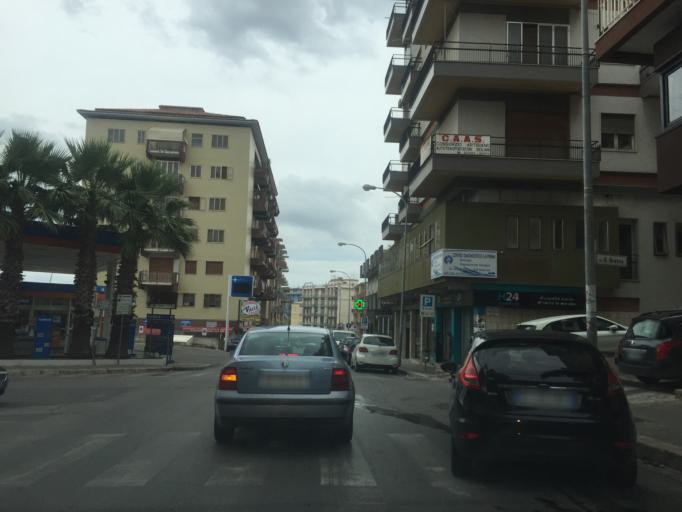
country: IT
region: Sicily
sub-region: Ragusa
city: Ragusa
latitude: 36.9175
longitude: 14.7292
